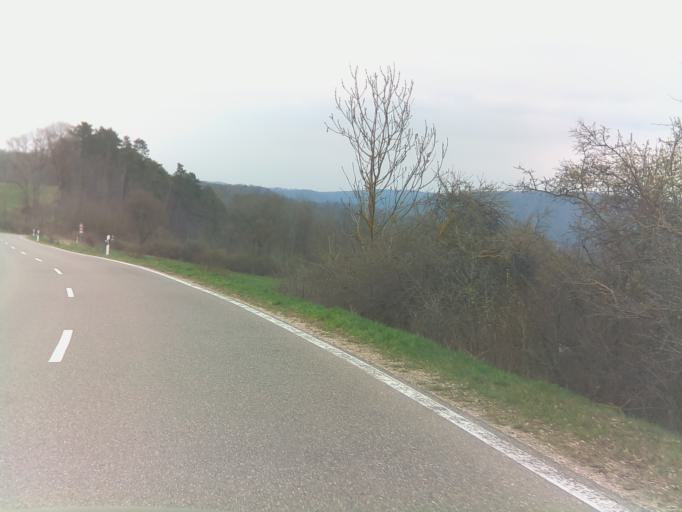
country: DE
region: Baden-Wuerttemberg
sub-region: Tuebingen Region
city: Schelklingen
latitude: 48.3856
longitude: 9.7115
